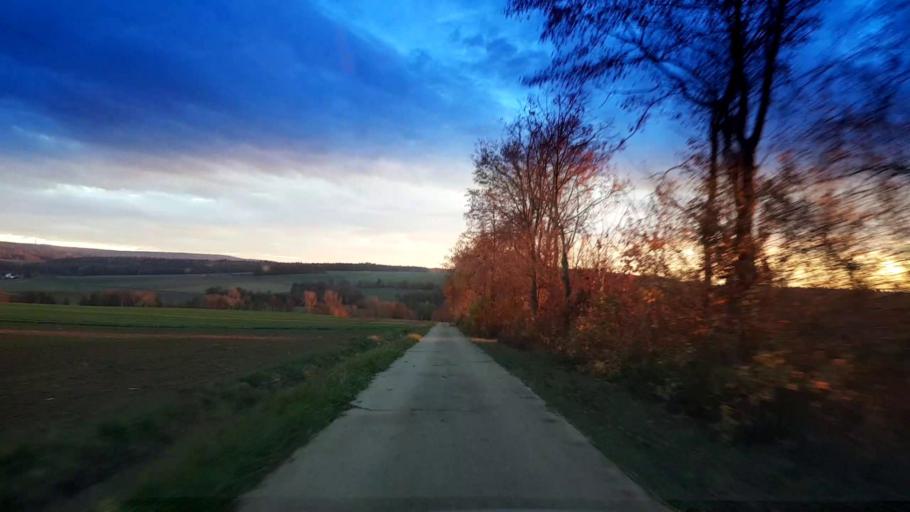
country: DE
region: Bavaria
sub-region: Upper Franconia
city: Memmelsdorf
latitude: 49.9504
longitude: 10.9804
